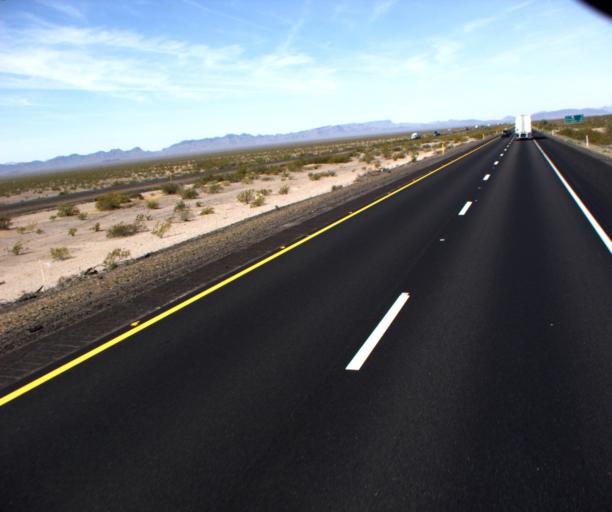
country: US
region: Arizona
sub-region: La Paz County
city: Salome
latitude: 33.6152
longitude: -113.6589
